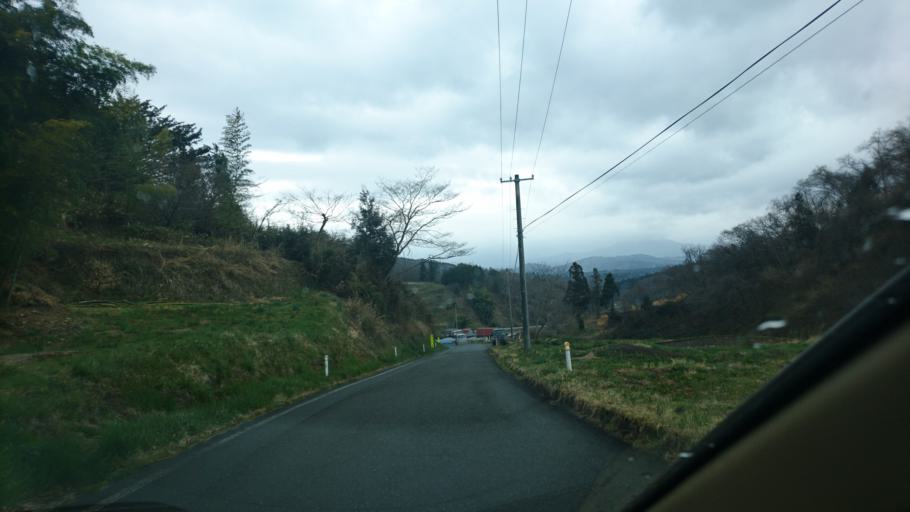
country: JP
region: Iwate
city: Ichinoseki
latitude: 38.9500
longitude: 141.3023
